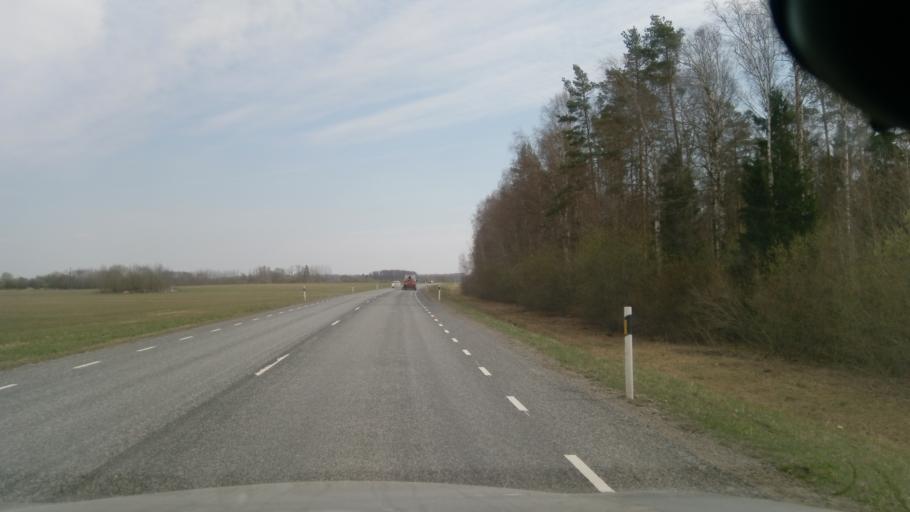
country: EE
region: Jaervamaa
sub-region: Tueri vald
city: Sarevere
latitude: 58.7785
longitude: 25.4959
